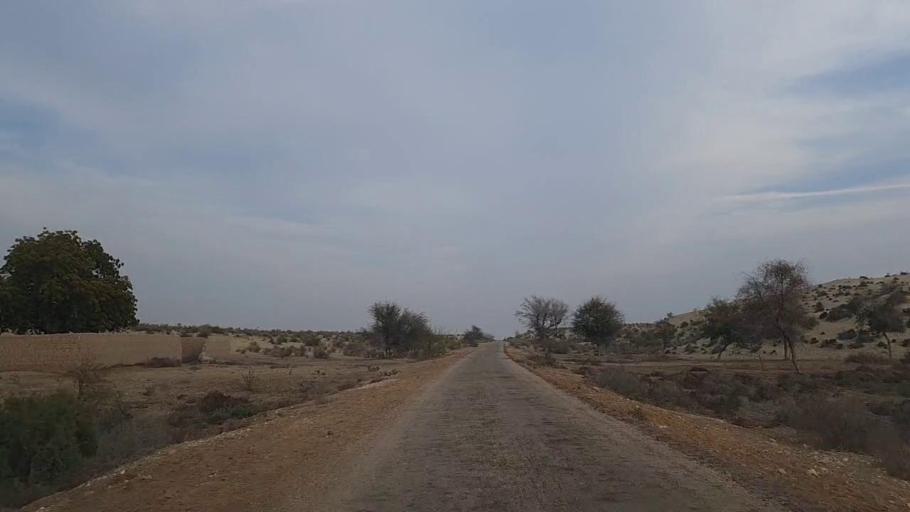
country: PK
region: Sindh
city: Daur
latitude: 26.5154
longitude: 68.4951
